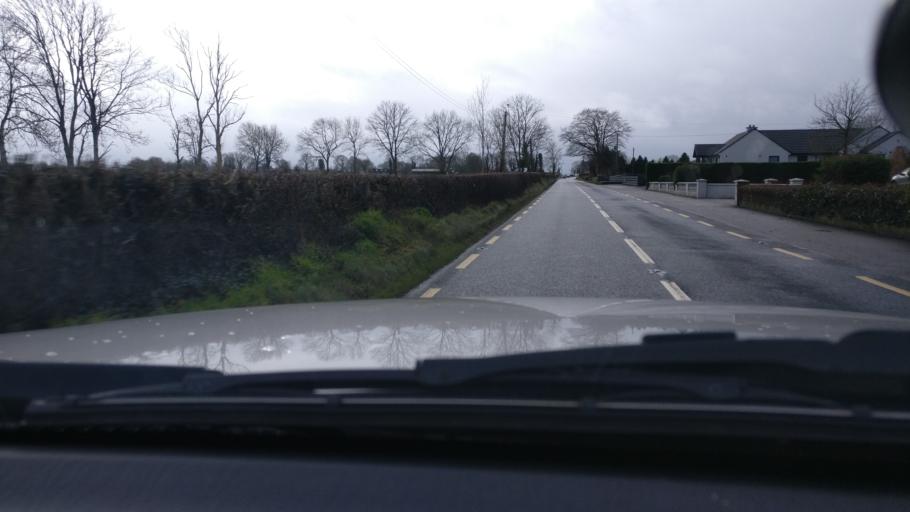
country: IE
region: Leinster
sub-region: An Longfort
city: Ballymahon
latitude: 53.5508
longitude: -7.7752
